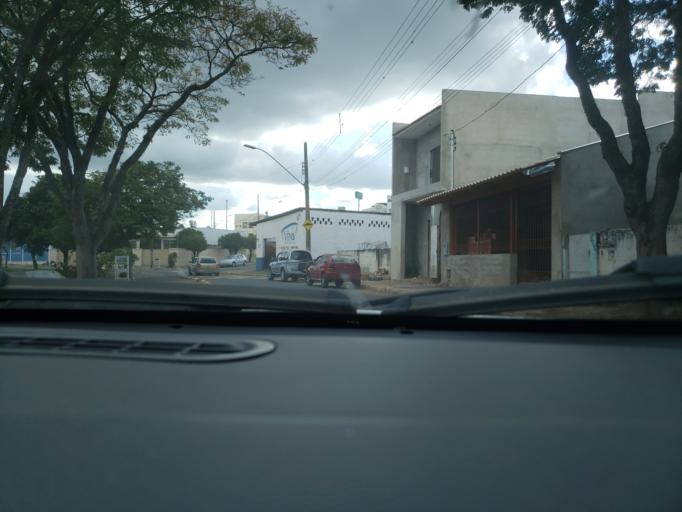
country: BR
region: Minas Gerais
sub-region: Campo Belo
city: Campo Belo
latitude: -20.8958
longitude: -45.2675
